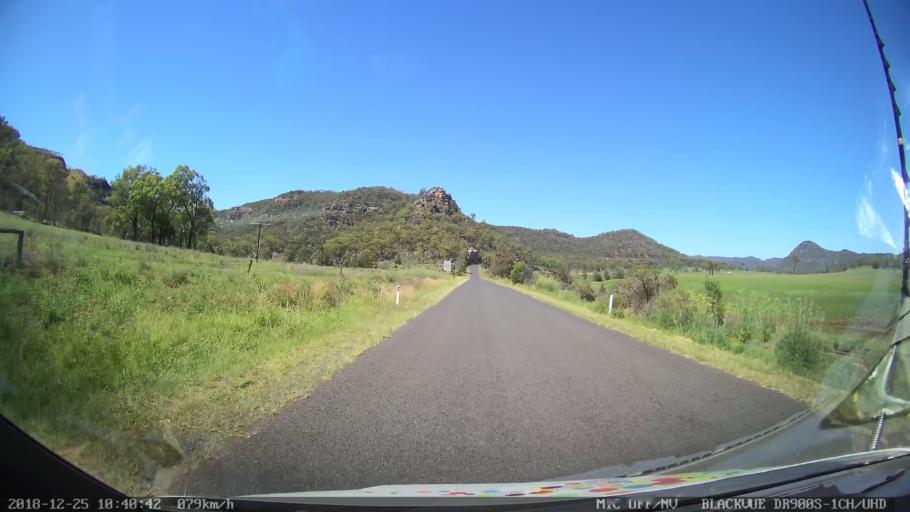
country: AU
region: New South Wales
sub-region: Upper Hunter Shire
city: Merriwa
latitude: -32.4102
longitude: 150.3414
